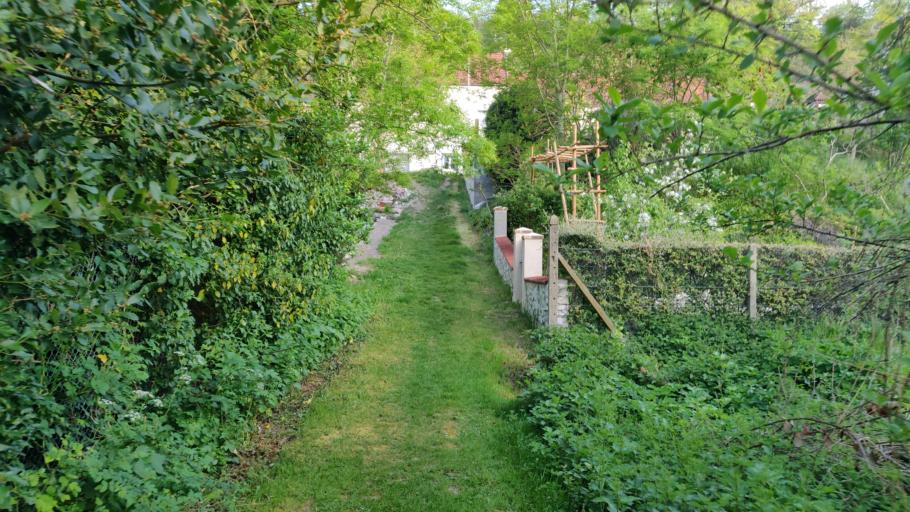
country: FR
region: Ile-de-France
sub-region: Departement des Yvelines
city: Freneuse
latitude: 49.0383
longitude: 1.6337
